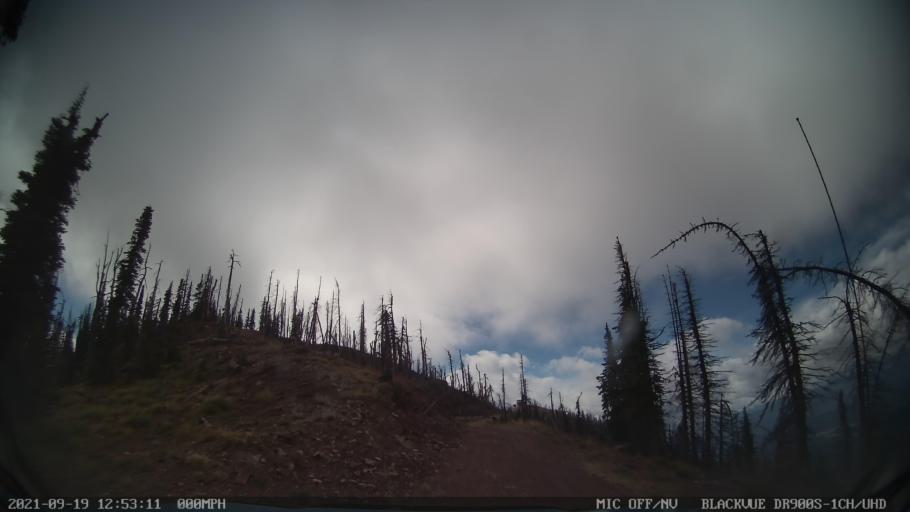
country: US
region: Montana
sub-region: Missoula County
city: Seeley Lake
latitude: 47.1936
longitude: -113.3562
